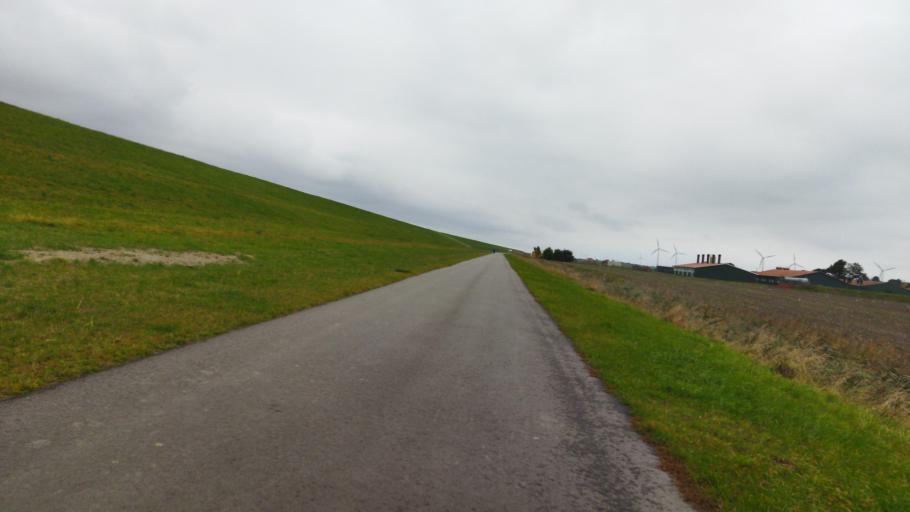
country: NL
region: Groningen
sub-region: Gemeente Delfzijl
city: Delfzijl
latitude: 53.4273
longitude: 7.0155
